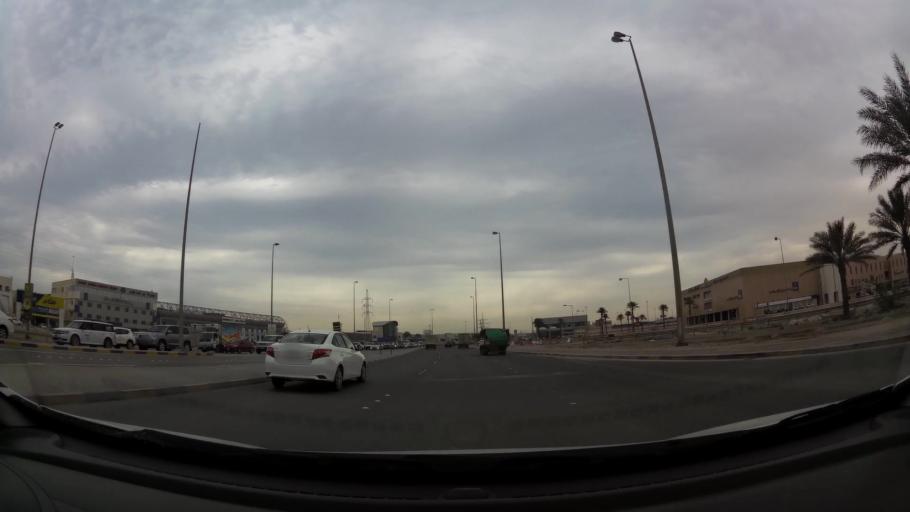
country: BH
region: Northern
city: Sitrah
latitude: 26.1717
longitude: 50.6011
